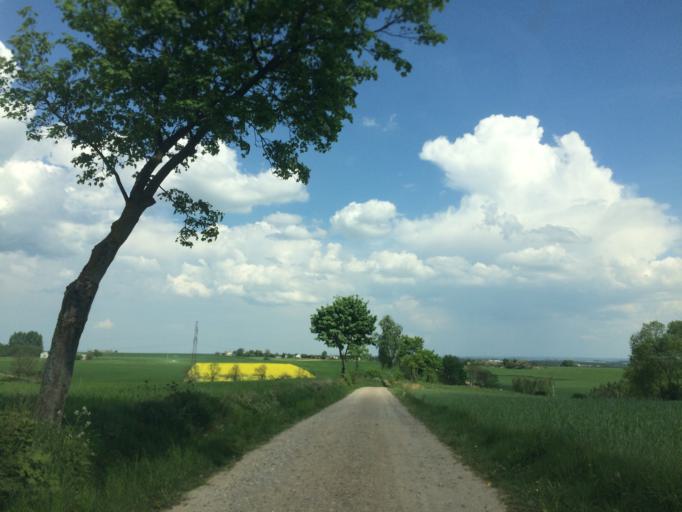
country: PL
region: Warmian-Masurian Voivodeship
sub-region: Powiat nowomiejski
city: Nowe Miasto Lubawskie
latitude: 53.4506
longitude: 19.5791
